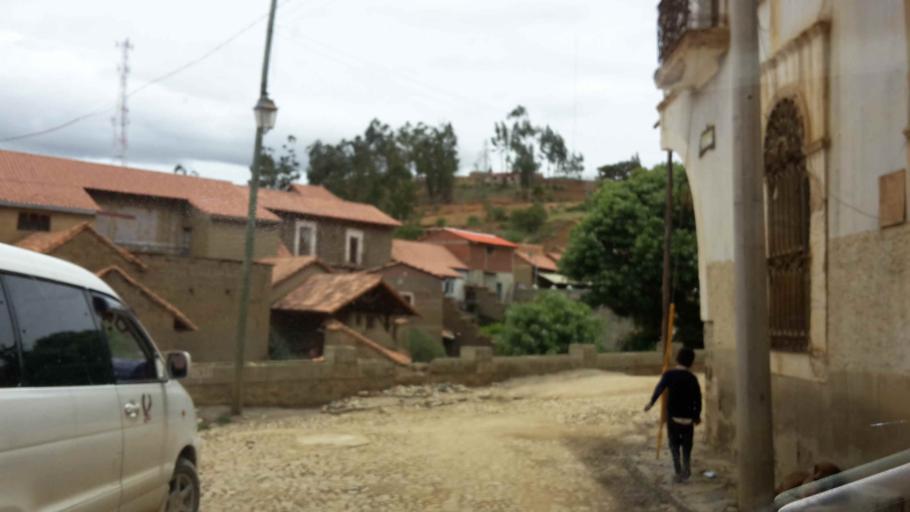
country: BO
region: Cochabamba
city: Totora
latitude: -17.7364
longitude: -65.1919
